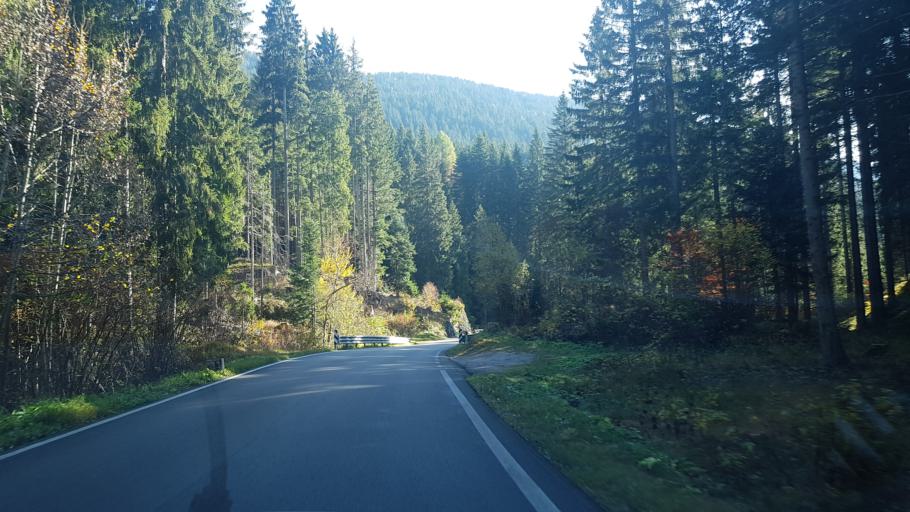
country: IT
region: Veneto
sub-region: Provincia di Belluno
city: Candide
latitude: 46.6293
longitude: 12.4652
